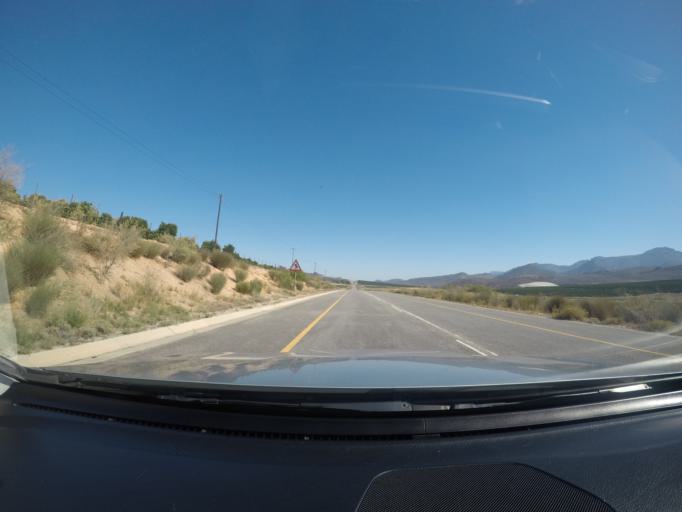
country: ZA
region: Western Cape
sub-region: West Coast District Municipality
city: Clanwilliam
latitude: -32.4880
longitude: 18.9647
